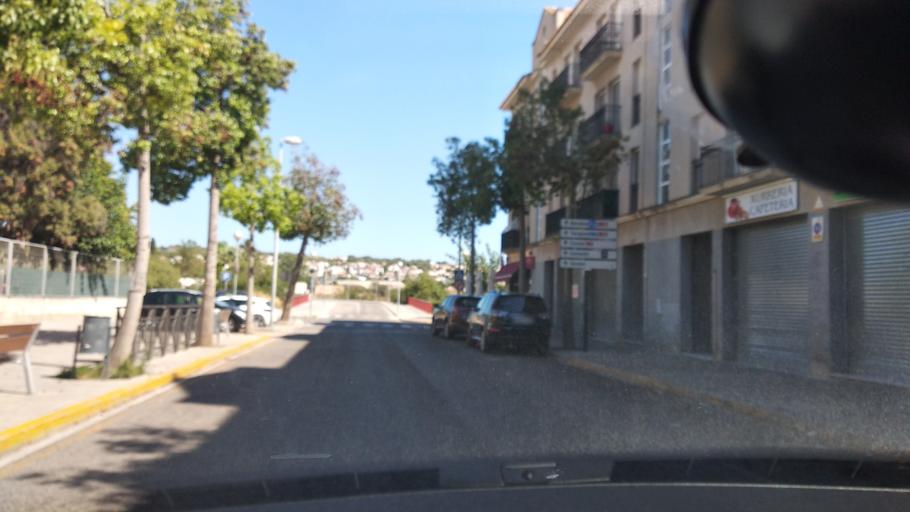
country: ES
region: Catalonia
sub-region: Provincia de Tarragona
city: El Vendrell
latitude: 41.2191
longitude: 1.5394
